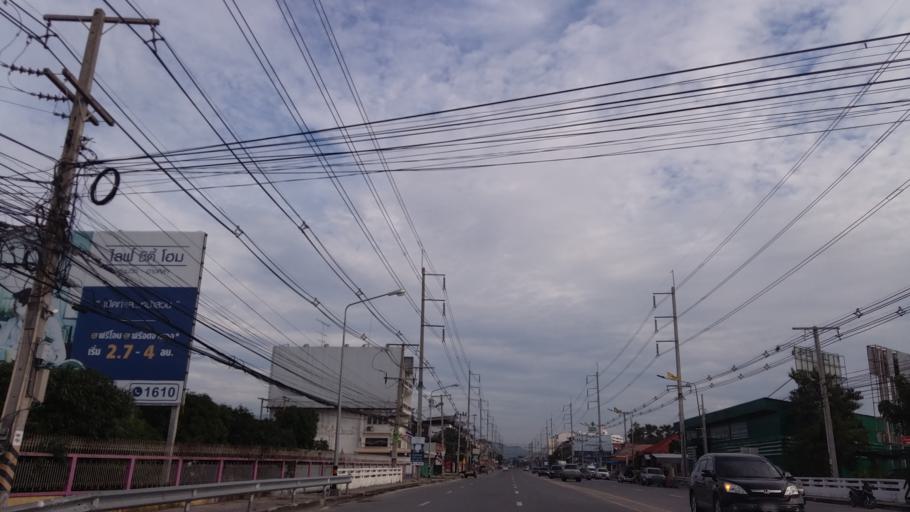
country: TH
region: Chon Buri
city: Chon Buri
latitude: 13.3240
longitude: 100.9434
